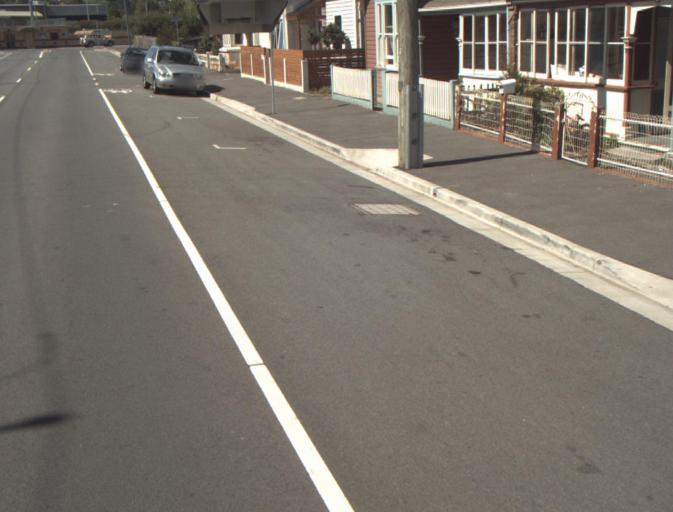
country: AU
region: Tasmania
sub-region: Launceston
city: West Launceston
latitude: -41.4465
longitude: 147.1374
